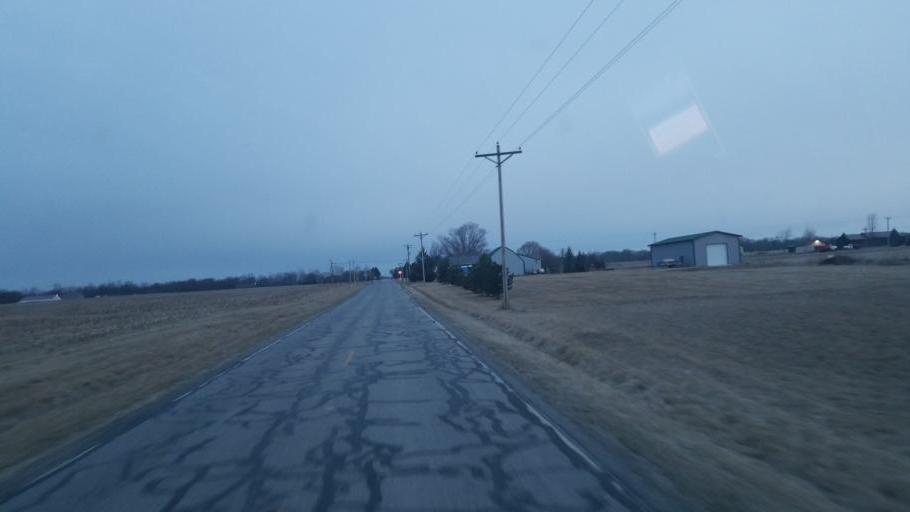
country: US
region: Ohio
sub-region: Defiance County
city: Hicksville
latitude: 41.3250
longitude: -84.7453
